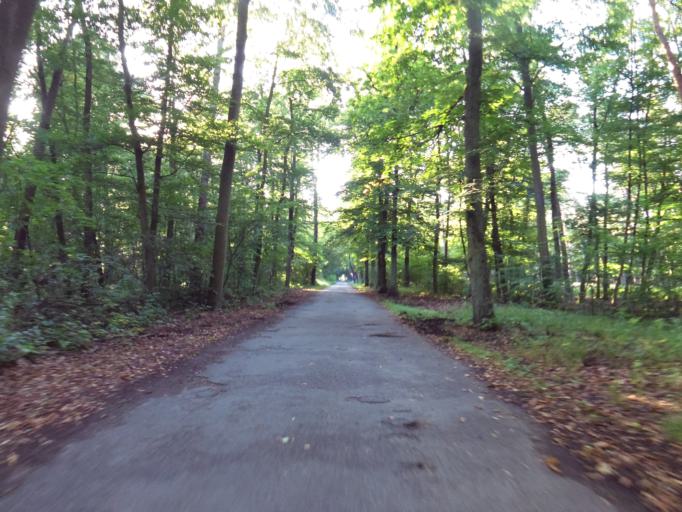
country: DE
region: Baden-Wuerttemberg
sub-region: Karlsruhe Region
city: Mannheim
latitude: 49.5343
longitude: 8.5206
